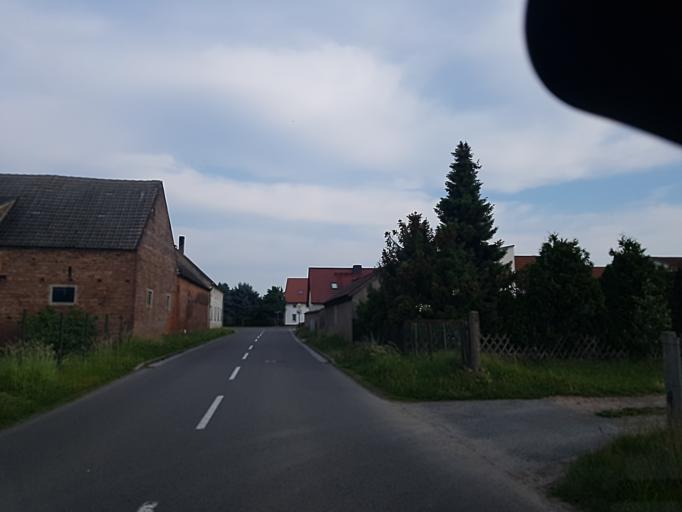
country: DE
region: Saxony-Anhalt
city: Jessen
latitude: 51.8335
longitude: 12.9428
